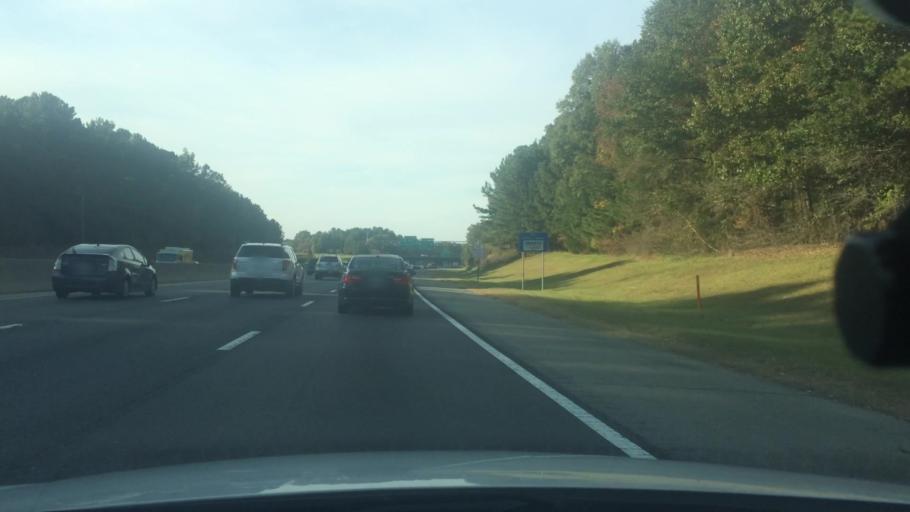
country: US
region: North Carolina
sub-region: Orange County
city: Chapel Hill
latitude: 35.9090
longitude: -78.9780
